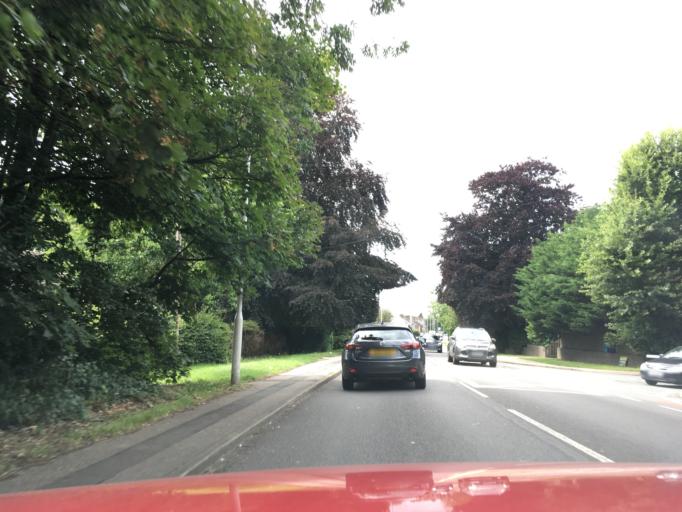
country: GB
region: England
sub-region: Surrey
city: Felbridge
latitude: 51.1352
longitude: -0.0294
